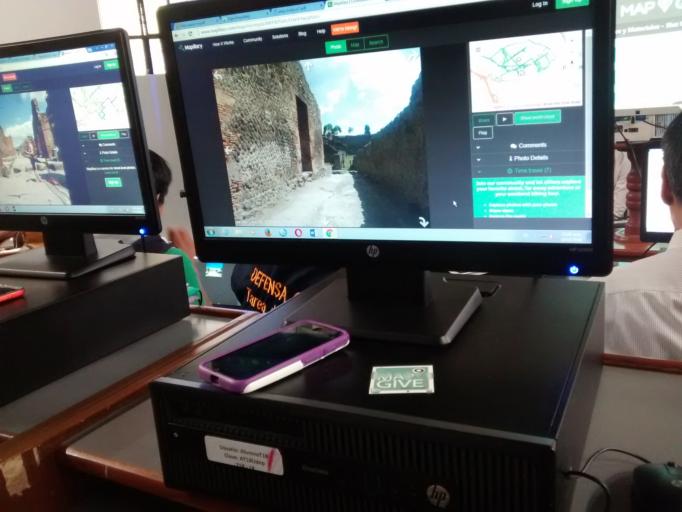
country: PE
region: Piura
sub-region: Provincia de Piura
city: Piura
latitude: -5.1770
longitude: -80.6360
